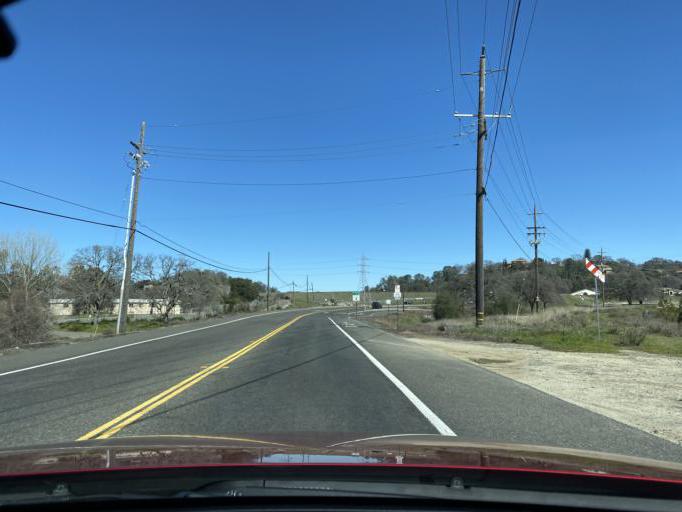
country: US
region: California
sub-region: Sacramento County
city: Folsom
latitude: 38.6918
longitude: -121.1458
